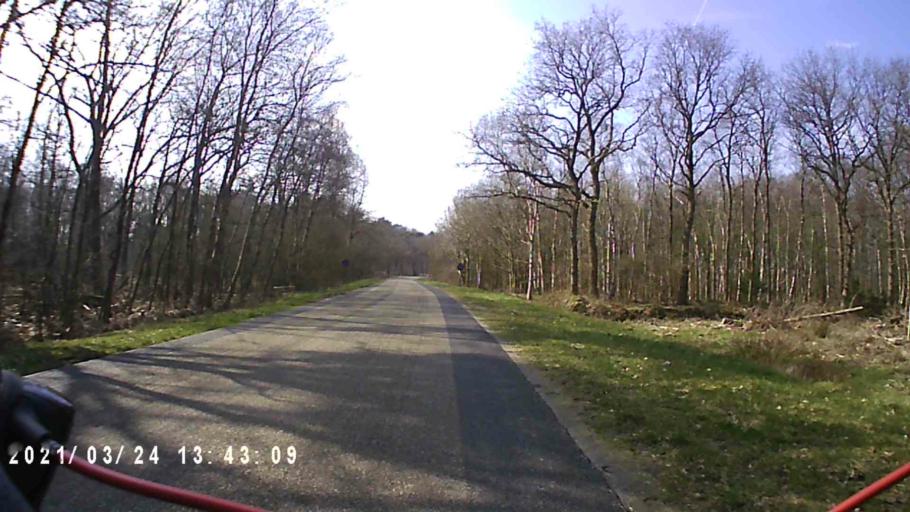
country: NL
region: Groningen
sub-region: Gemeente Grootegast
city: Grootegast
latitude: 53.0865
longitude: 6.2731
